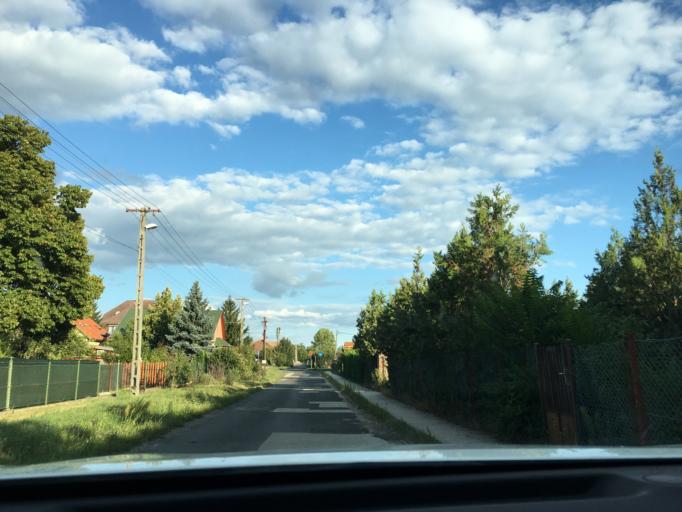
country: HU
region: Budapest
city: Budapest XVII. keruelet
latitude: 47.4715
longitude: 19.2581
